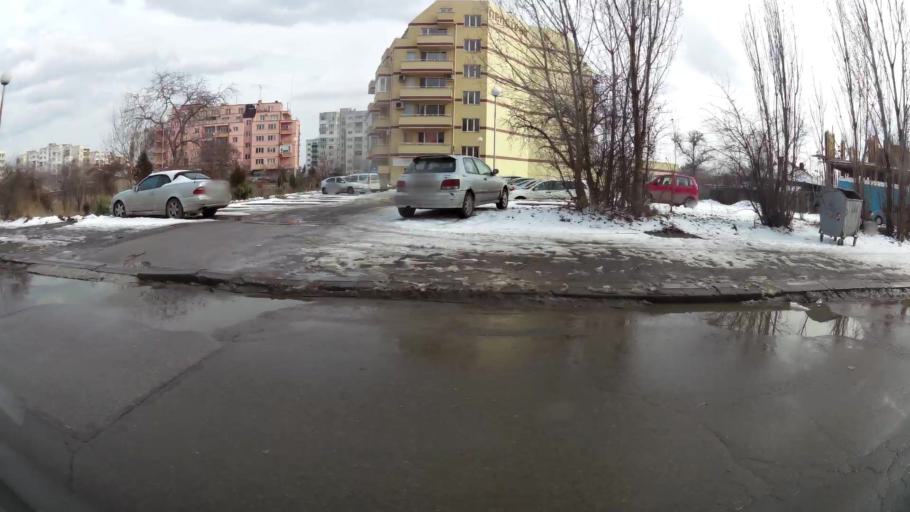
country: BG
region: Sofia-Capital
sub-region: Stolichna Obshtina
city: Sofia
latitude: 42.7082
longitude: 23.3837
